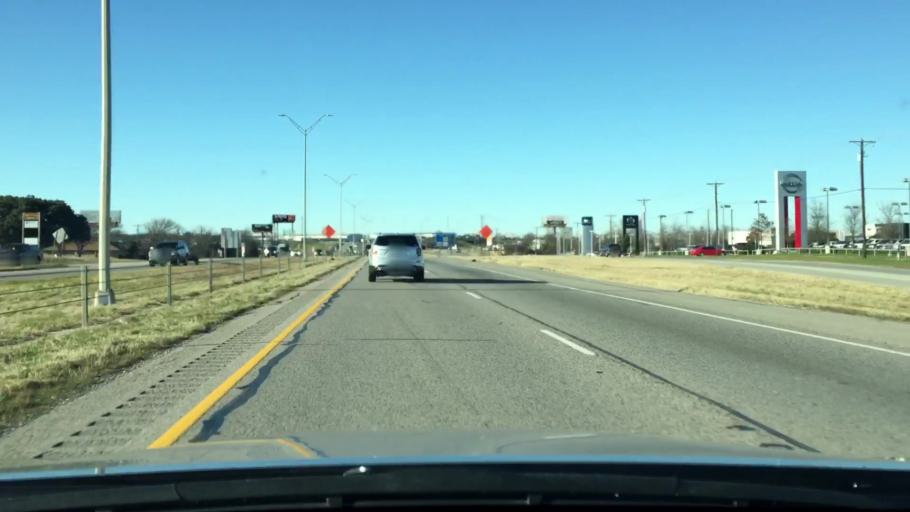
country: US
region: Texas
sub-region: Johnson County
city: Burleson
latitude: 32.5466
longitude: -97.3161
